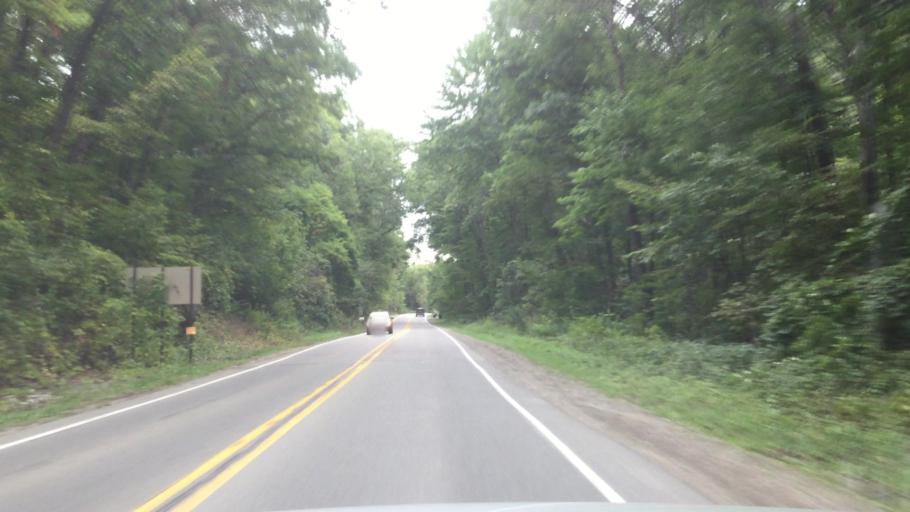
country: US
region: Michigan
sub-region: Livingston County
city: Whitmore Lake
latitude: 42.4631
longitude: -83.7962
